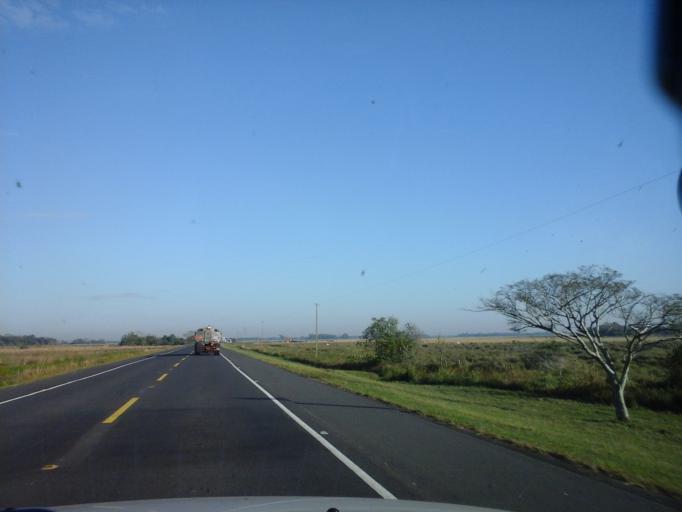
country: PY
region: Neembucu
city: Pilar
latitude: -26.8717
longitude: -57.9218
